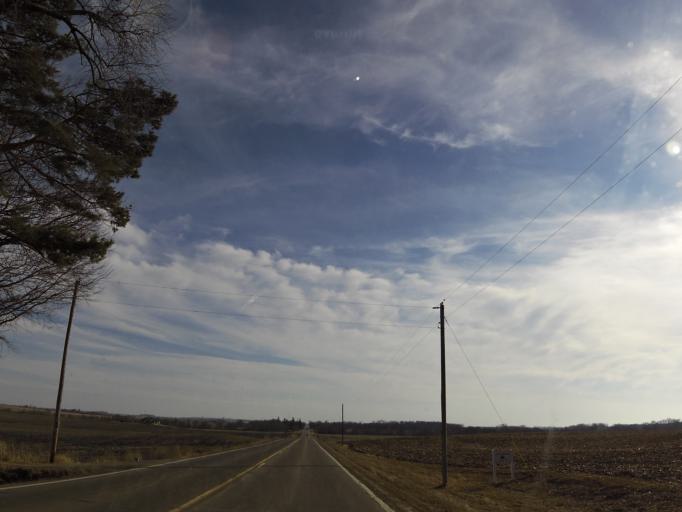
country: US
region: Minnesota
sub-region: Rice County
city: Northfield
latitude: 44.5292
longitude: -93.2010
